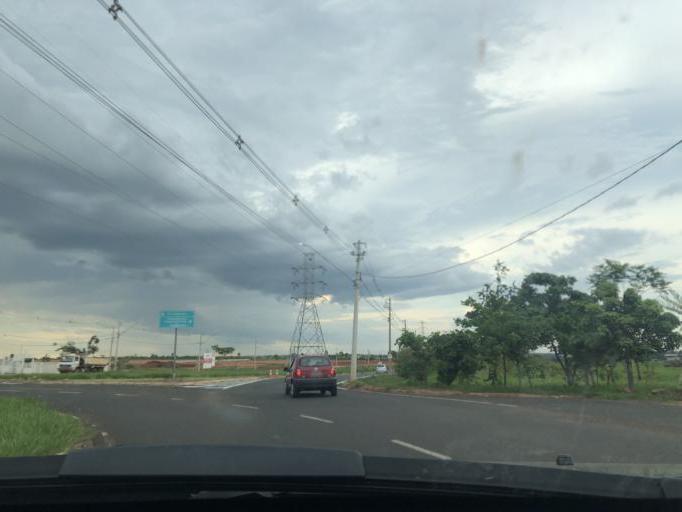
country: BR
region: Sao Paulo
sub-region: Sao Jose Do Rio Preto
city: Sao Jose do Rio Preto
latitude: -20.8377
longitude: -49.4198
